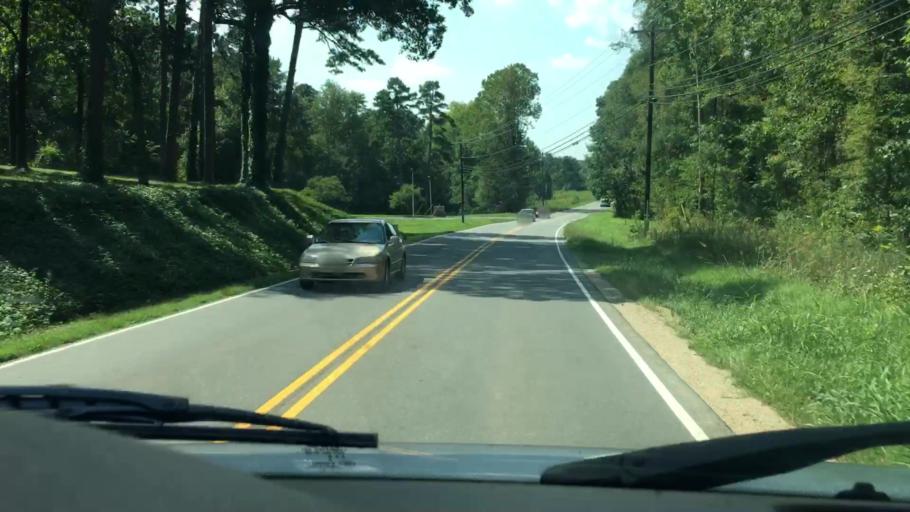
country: US
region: North Carolina
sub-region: Mecklenburg County
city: Huntersville
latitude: 35.3484
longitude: -80.8816
